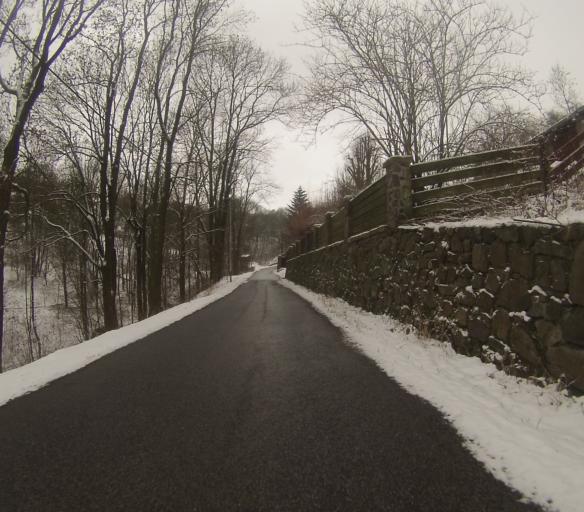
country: CZ
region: Ustecky
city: Benesov nad Ploucnici
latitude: 50.7337
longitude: 14.2585
